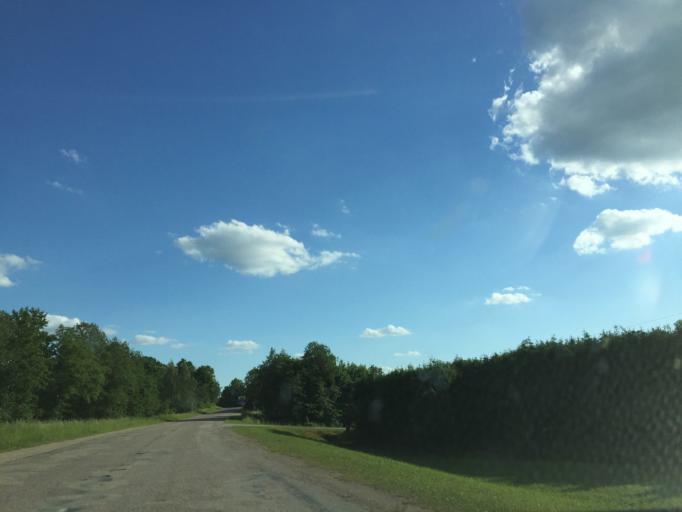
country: LV
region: Kandava
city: Kandava
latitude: 56.8408
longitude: 22.7466
